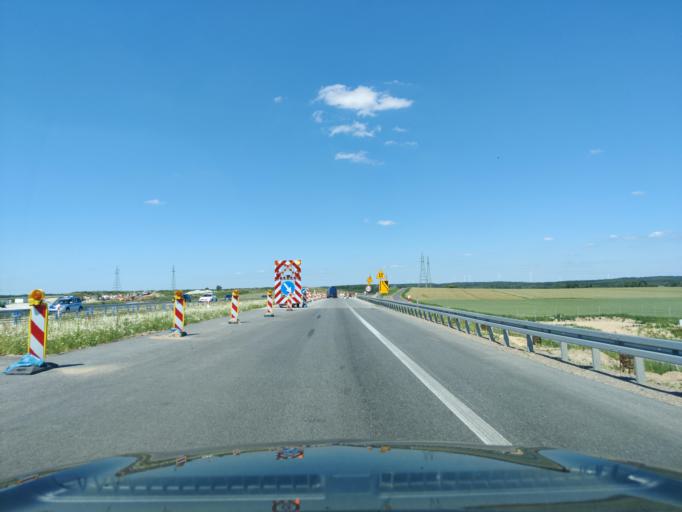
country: PL
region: Masovian Voivodeship
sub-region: Powiat mlawski
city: Mlawa
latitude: 53.1202
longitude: 20.4105
